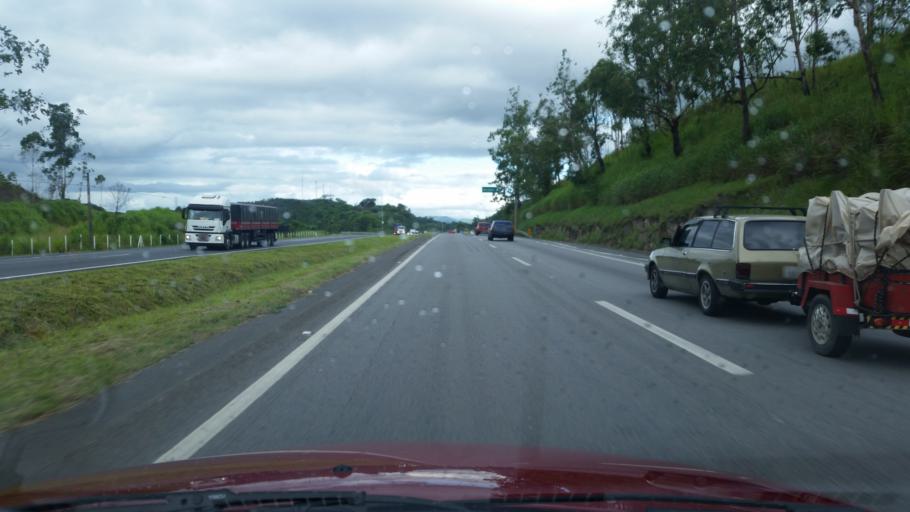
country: BR
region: Sao Paulo
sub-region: Miracatu
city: Miracatu
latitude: -24.2706
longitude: -47.4009
